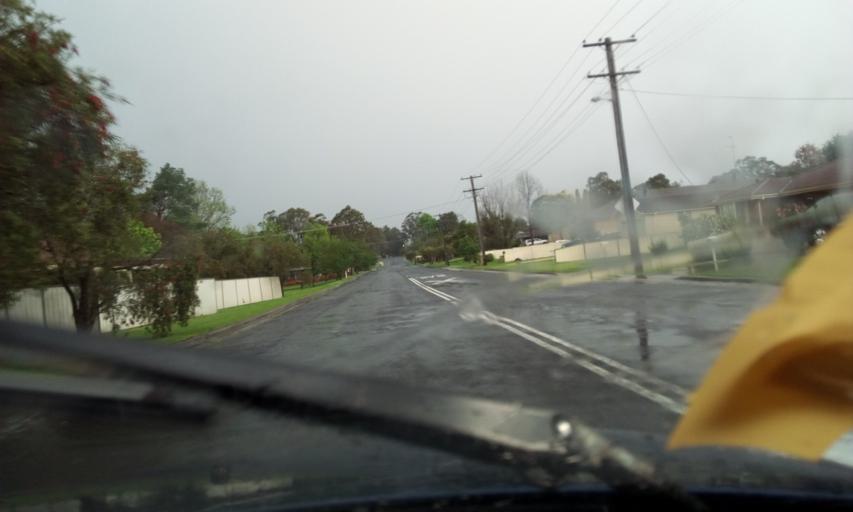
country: AU
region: New South Wales
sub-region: Wollondilly
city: Douglas Park
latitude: -34.1840
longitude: 150.7108
